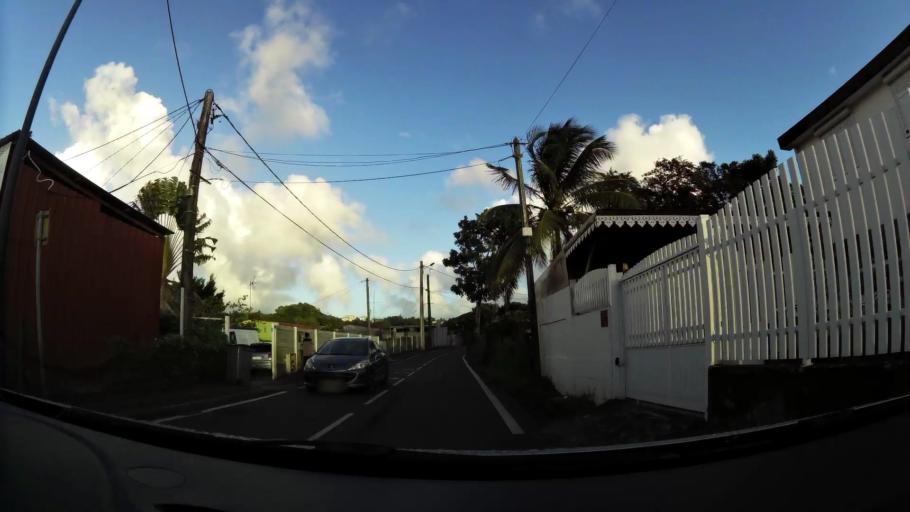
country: MQ
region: Martinique
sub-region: Martinique
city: Fort-de-France
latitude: 14.6360
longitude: -61.0705
